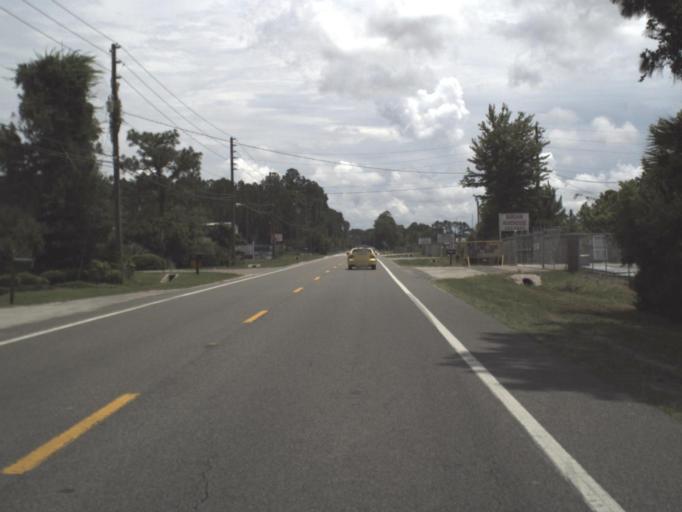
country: US
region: Florida
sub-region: Nassau County
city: Yulee
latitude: 30.6204
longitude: -81.5987
